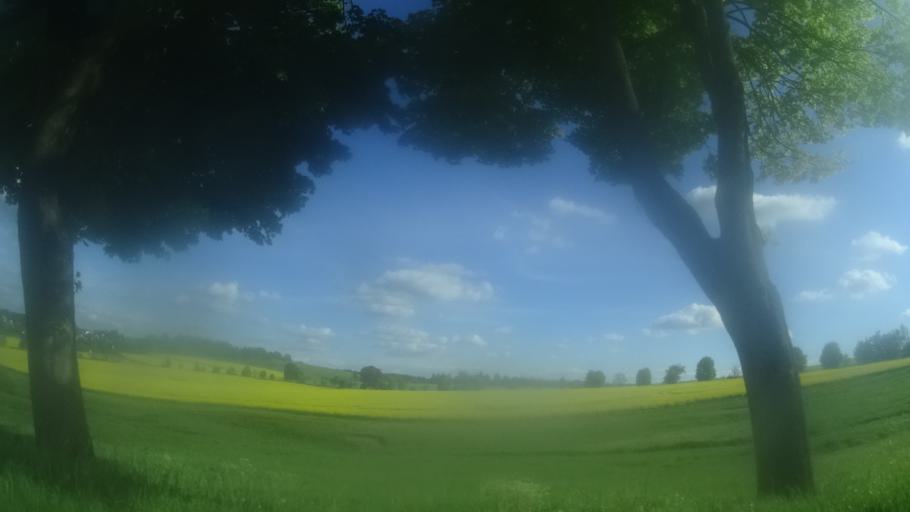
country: DE
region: Thuringia
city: Herschdorf
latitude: 50.6237
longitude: 11.0593
